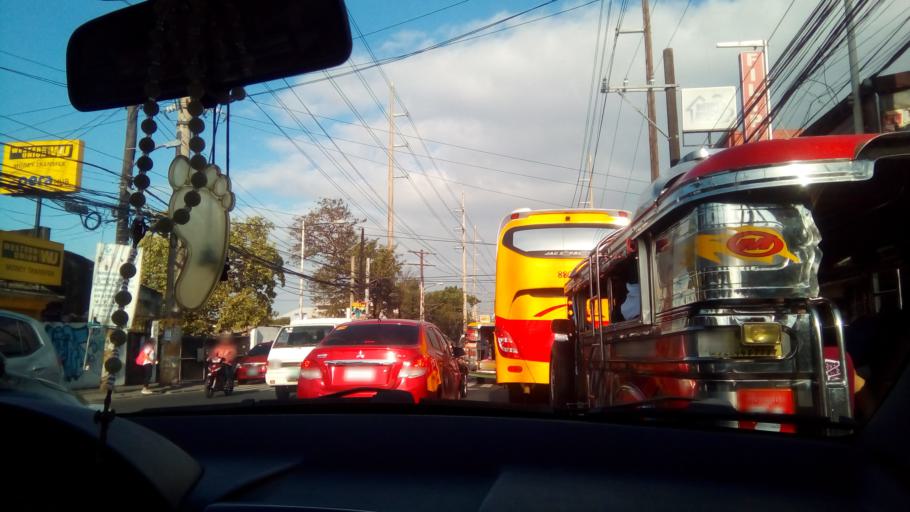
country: PH
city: Sambayanihan People's Village
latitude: 14.4363
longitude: 121.0079
